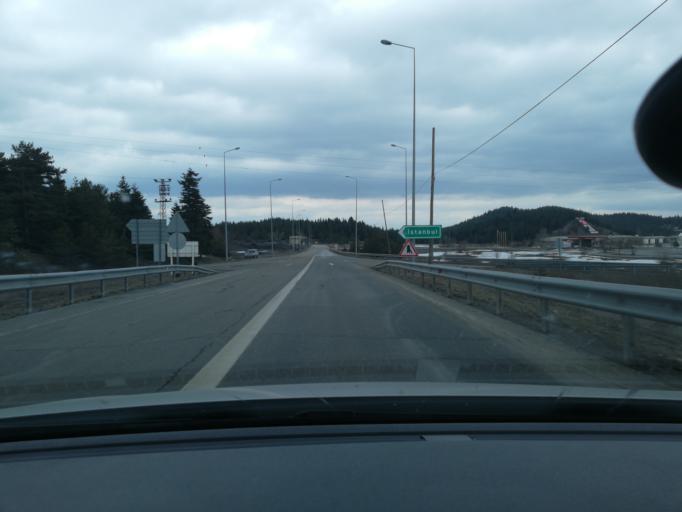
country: TR
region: Bolu
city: Gerede
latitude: 40.6126
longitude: 32.2533
